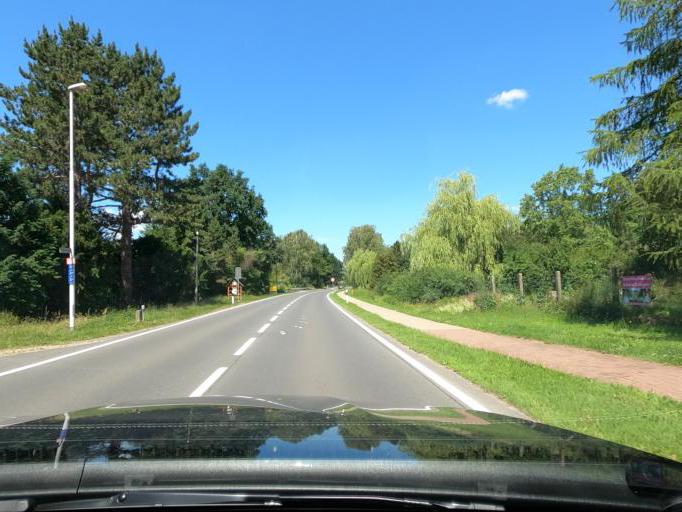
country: DE
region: Lower Saxony
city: Lehrte
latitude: 52.4036
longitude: 9.9742
